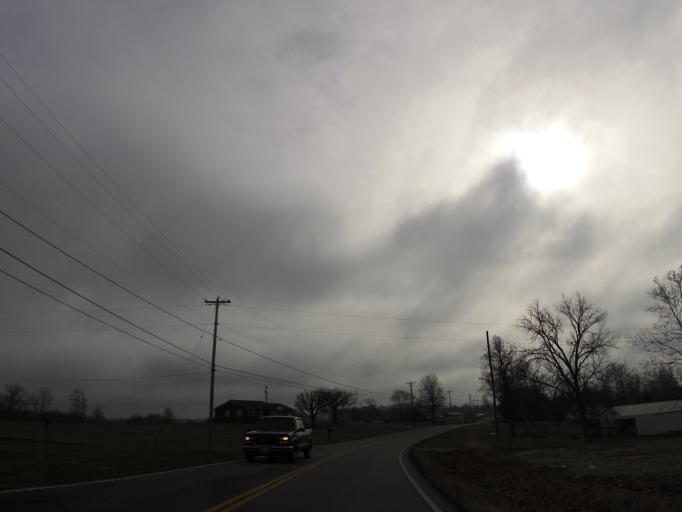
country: US
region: Kentucky
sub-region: Trimble County
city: Bedford
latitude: 38.6302
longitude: -85.3209
